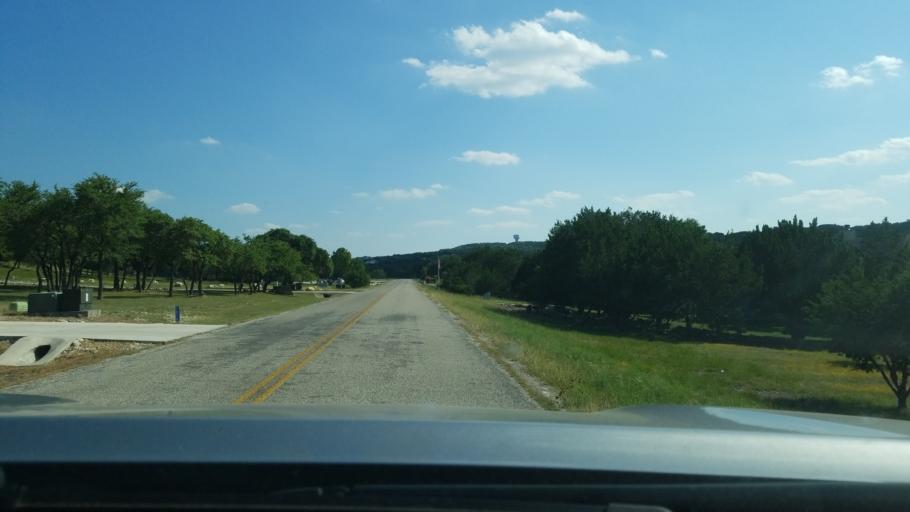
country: US
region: Texas
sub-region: Comal County
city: Bulverde
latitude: 29.8294
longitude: -98.3977
